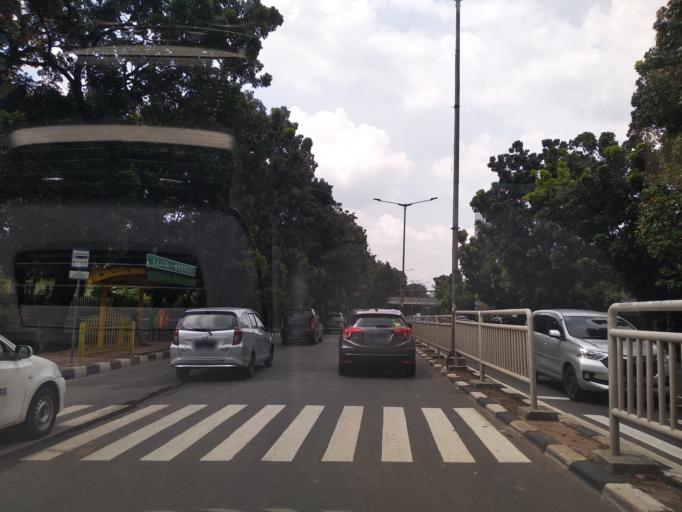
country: ID
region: Jakarta Raya
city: Jakarta
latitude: -6.2324
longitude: 106.8451
